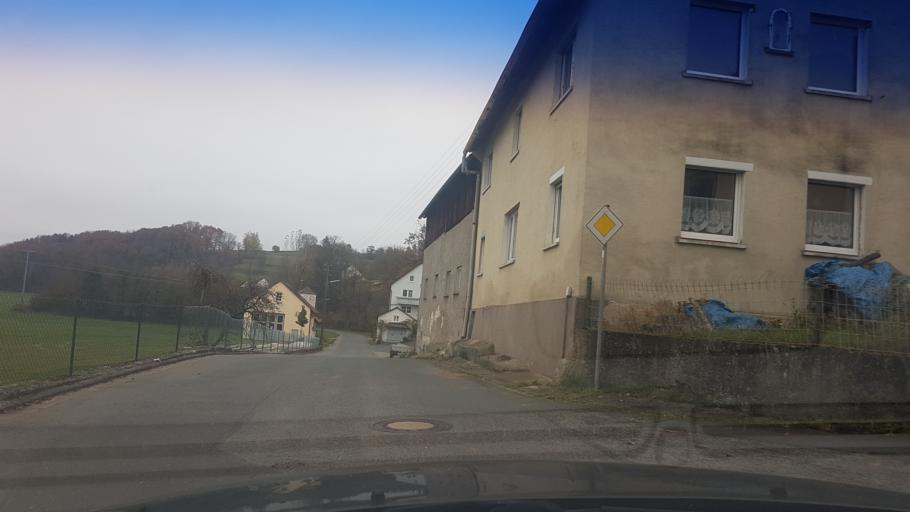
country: DE
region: Bavaria
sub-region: Upper Franconia
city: Rattelsdorf
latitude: 50.0485
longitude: 10.8719
